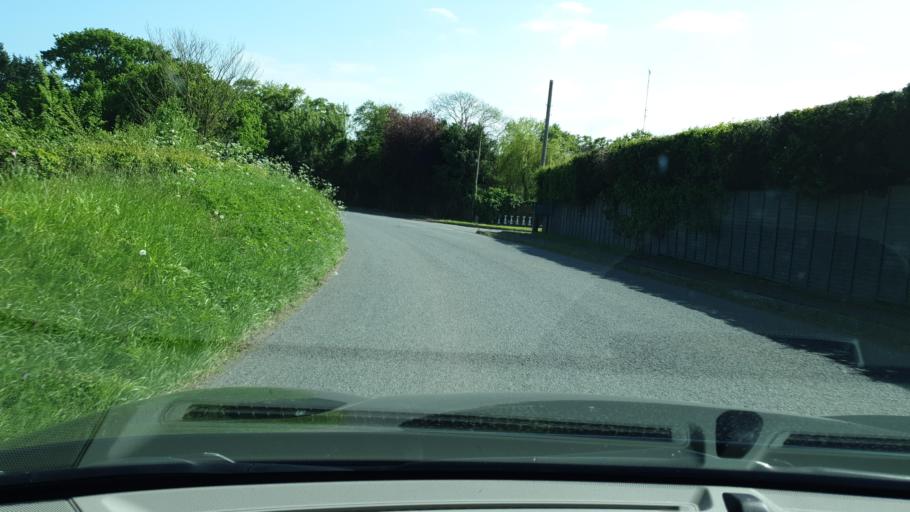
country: IE
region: Leinster
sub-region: Kildare
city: Maynooth
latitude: 53.4217
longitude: -6.5766
